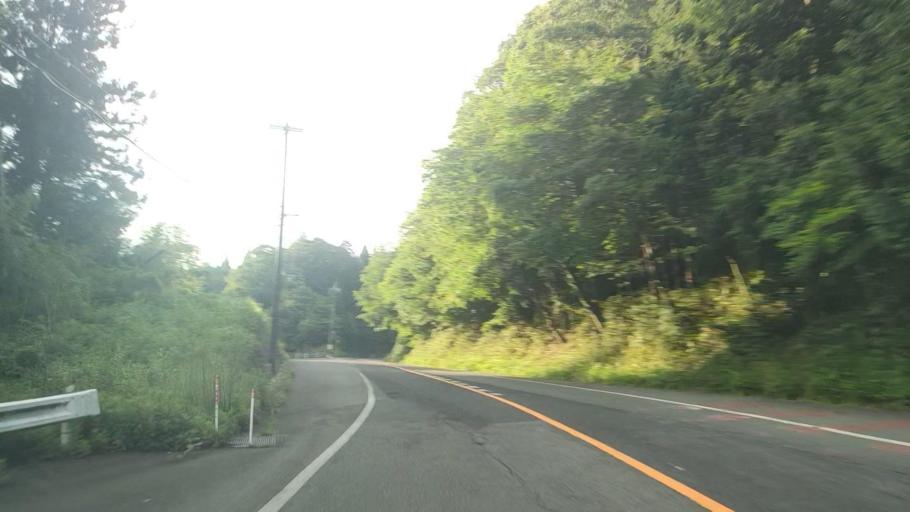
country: JP
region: Tottori
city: Kurayoshi
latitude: 35.2835
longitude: 133.6376
